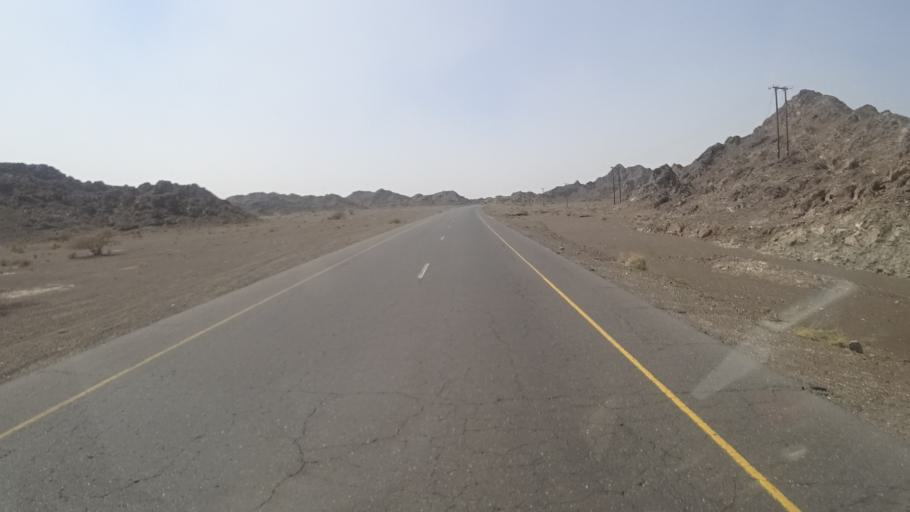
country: OM
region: Ash Sharqiyah
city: Ibra'
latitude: 22.6204
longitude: 58.3162
